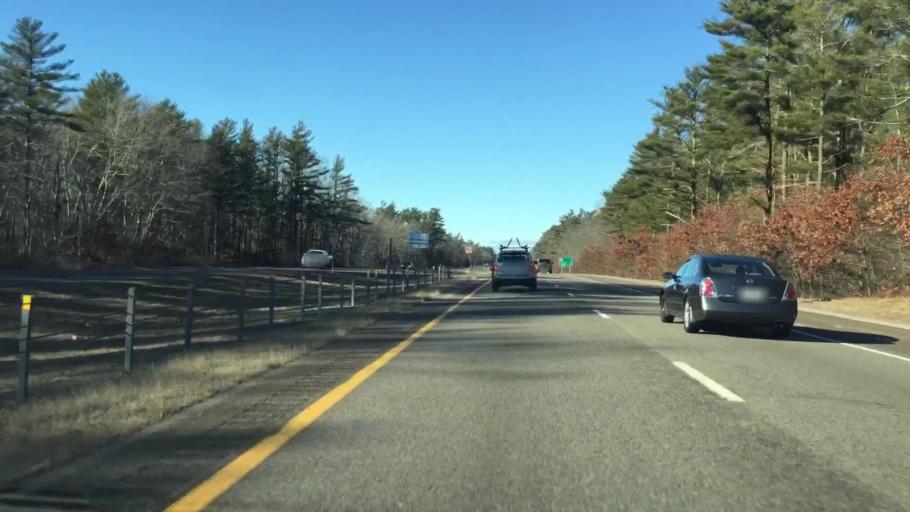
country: US
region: Massachusetts
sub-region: Plymouth County
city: Middleborough Center
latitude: 41.8510
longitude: -70.8616
